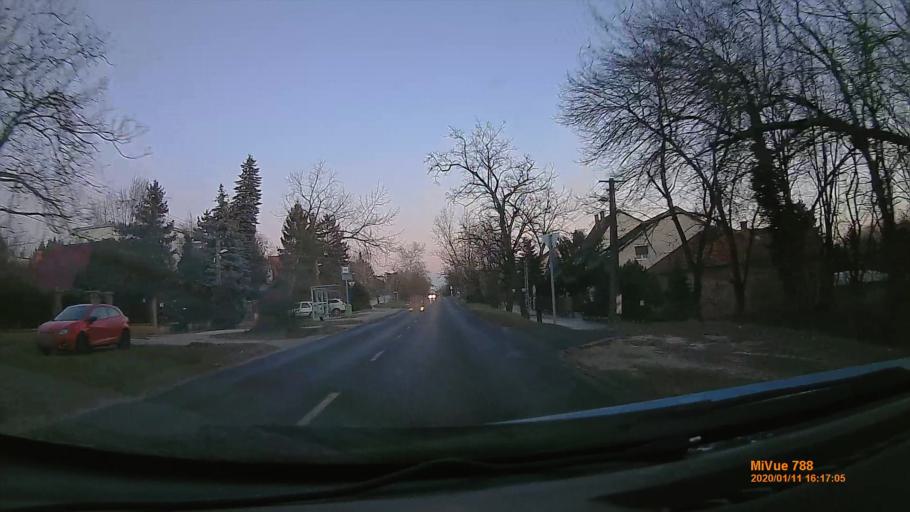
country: HU
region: Pest
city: Csomor
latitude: 47.5238
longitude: 19.2077
